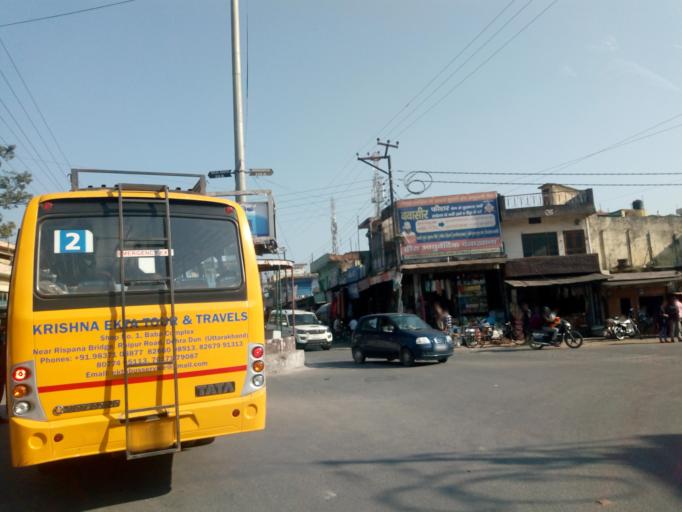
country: IN
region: Uttarakhand
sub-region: Dehradun
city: Harbatpur
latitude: 30.4387
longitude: 77.7380
